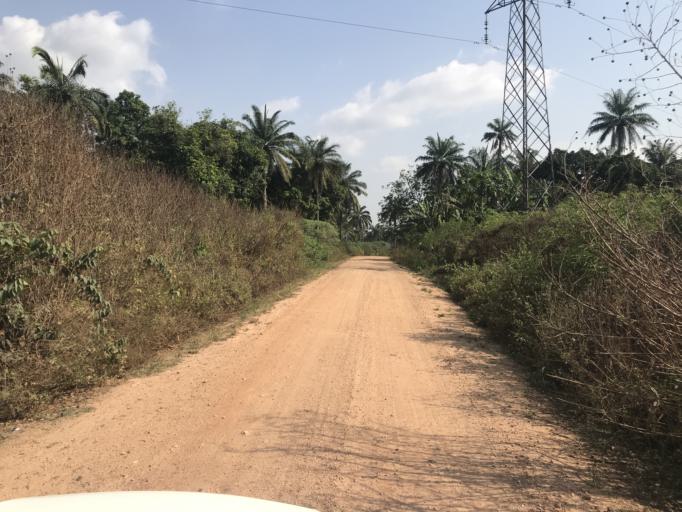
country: NG
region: Osun
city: Ikirun
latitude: 7.8683
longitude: 4.5862
